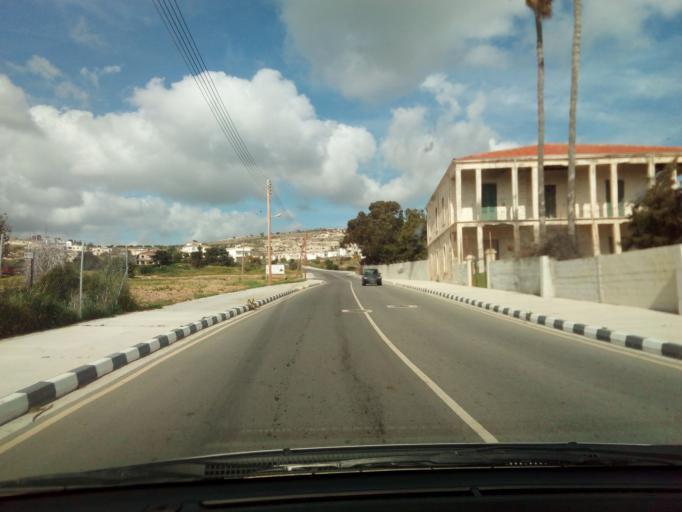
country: CY
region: Pafos
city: Paphos
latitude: 34.7642
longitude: 32.4556
